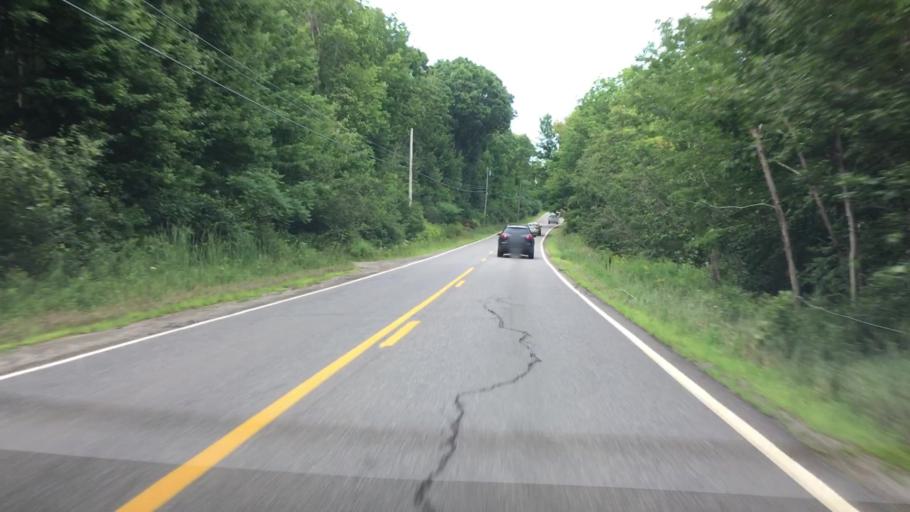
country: US
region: Maine
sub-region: Waldo County
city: Belfast
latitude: 44.3616
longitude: -69.0450
